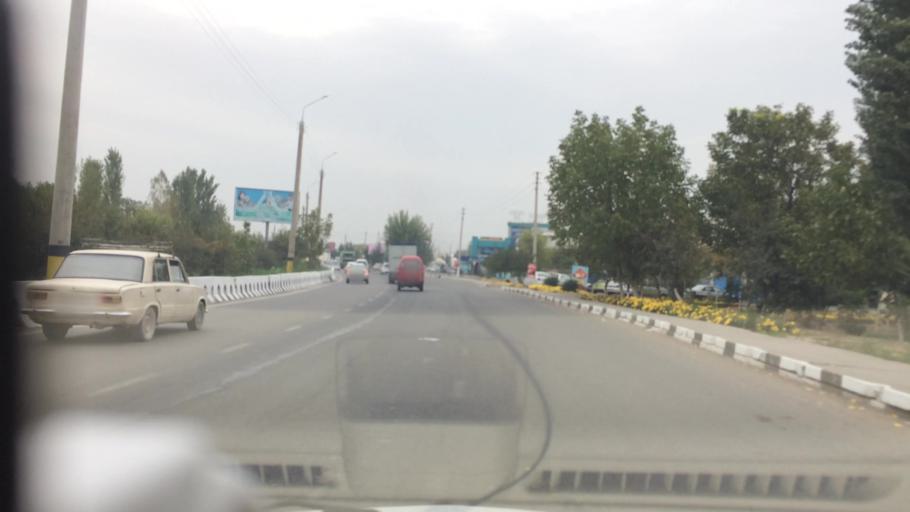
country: UZ
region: Toshkent
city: Salor
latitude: 41.3072
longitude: 69.3426
